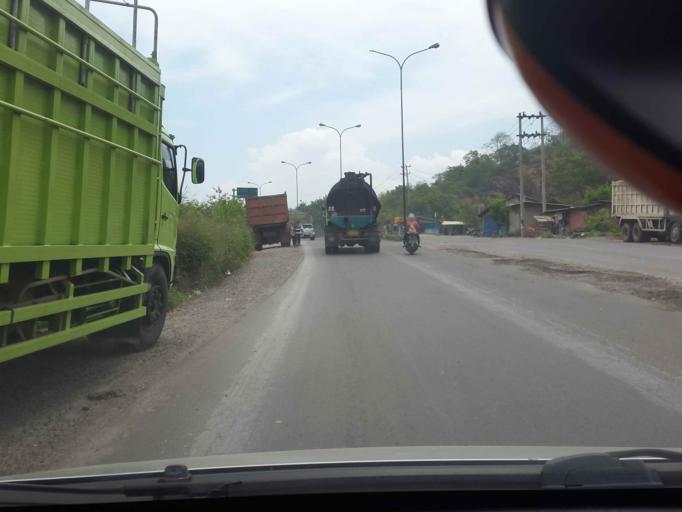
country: ID
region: Lampung
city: Panjang
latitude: -5.4438
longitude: 105.3119
